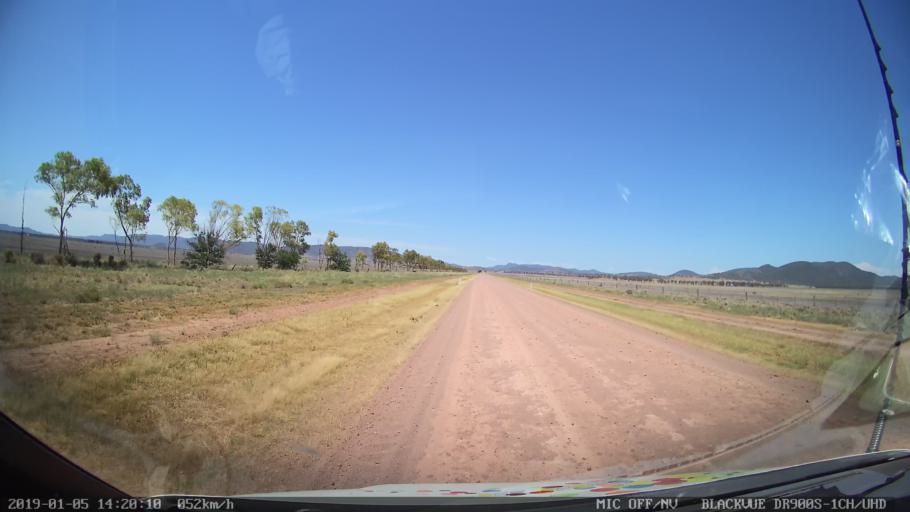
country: AU
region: New South Wales
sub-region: Liverpool Plains
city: Quirindi
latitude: -31.2494
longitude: 150.5023
